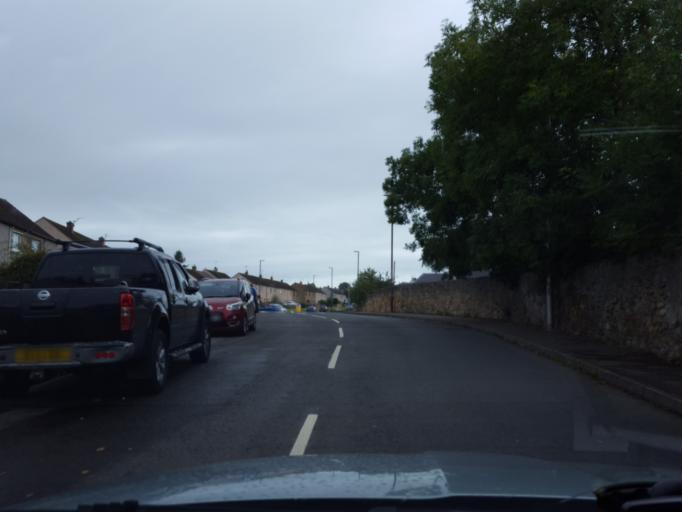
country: GB
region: Scotland
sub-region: Midlothian
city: Bonnyrigg
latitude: 55.8750
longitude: -3.1200
